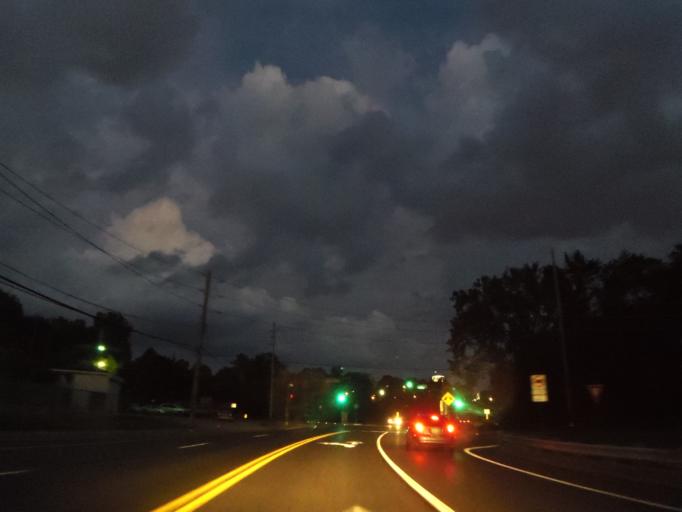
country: US
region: Missouri
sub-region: Saint Louis County
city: Saint George
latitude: 38.5275
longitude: -90.3009
